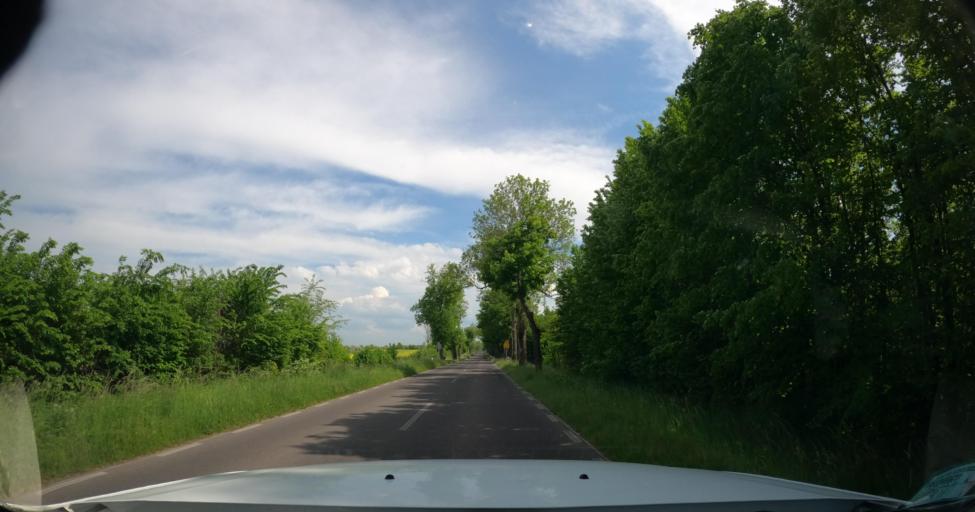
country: PL
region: Warmian-Masurian Voivodeship
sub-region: Powiat lidzbarski
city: Lidzbark Warminski
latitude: 54.1447
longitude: 20.5625
